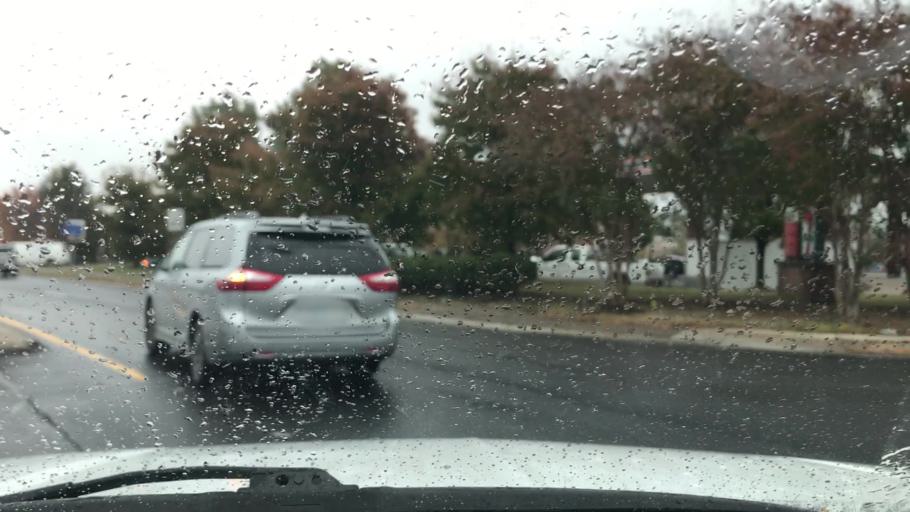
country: US
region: Virginia
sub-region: Henrico County
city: Short Pump
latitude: 37.6516
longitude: -77.6117
